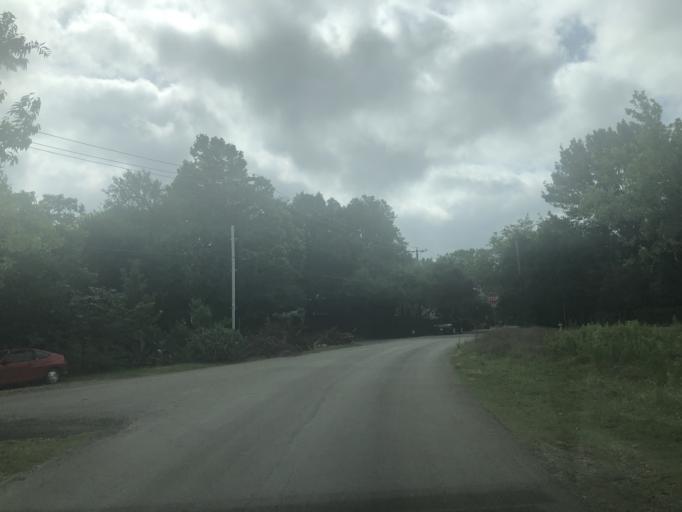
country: US
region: Texas
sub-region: Dallas County
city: University Park
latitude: 32.8570
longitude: -96.8353
